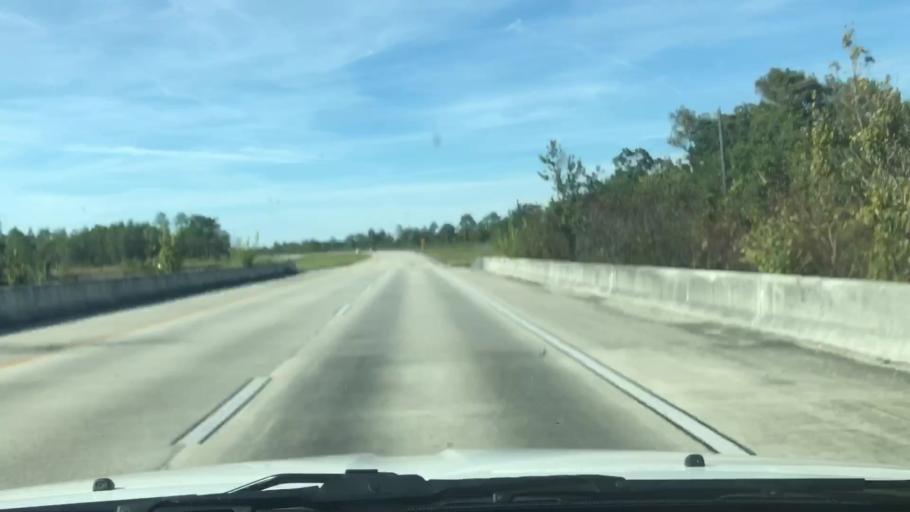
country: US
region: Florida
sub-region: Indian River County
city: Fellsmere
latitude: 27.6884
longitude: -80.8801
